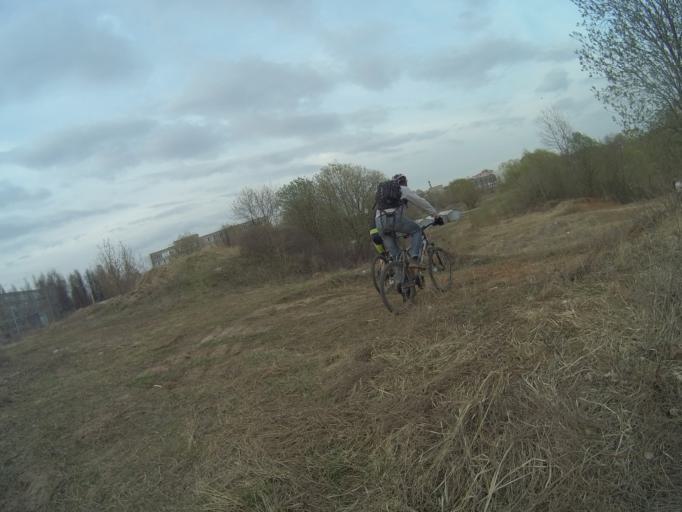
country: RU
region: Vladimir
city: Vladimir
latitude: 56.1440
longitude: 40.3726
